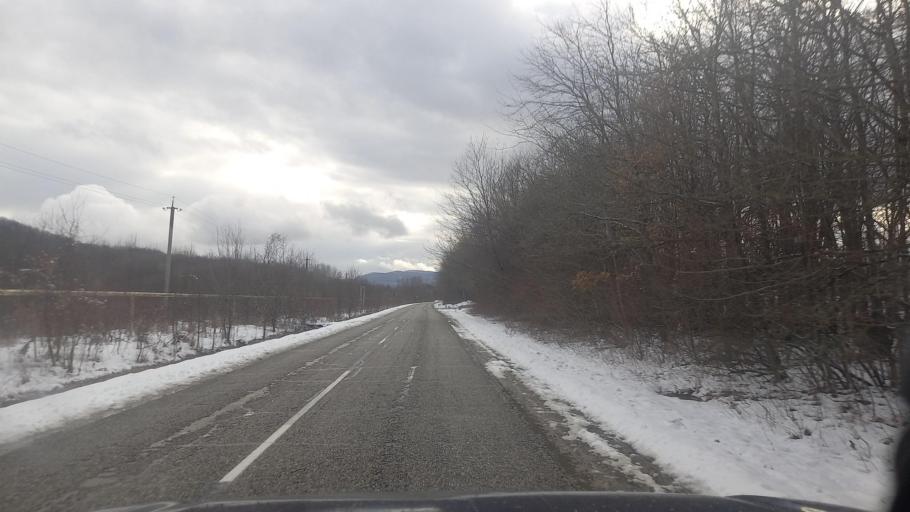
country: RU
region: Krasnodarskiy
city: Smolenskaya
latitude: 44.7466
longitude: 38.8398
